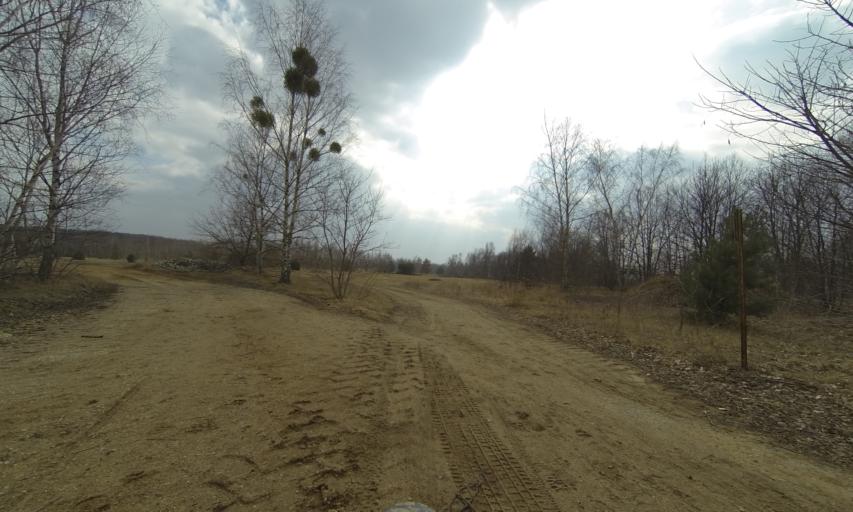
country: DE
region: Saxony
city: Albertstadt
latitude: 51.0994
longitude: 13.7442
